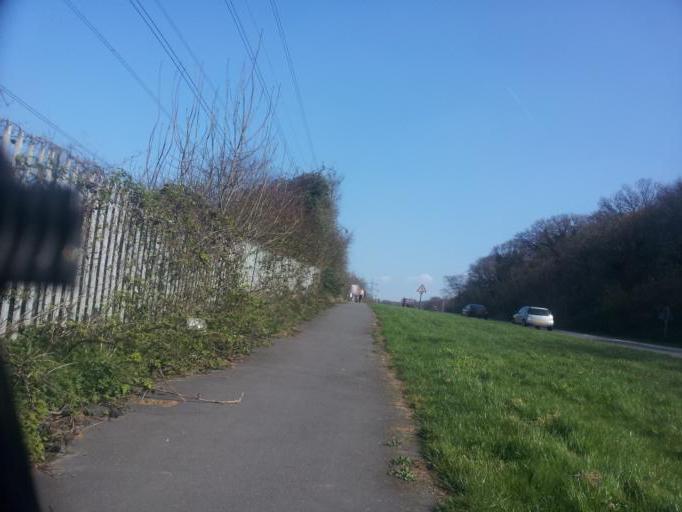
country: GB
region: England
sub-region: Kent
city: Greenhithe
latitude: 51.4337
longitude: 0.2829
